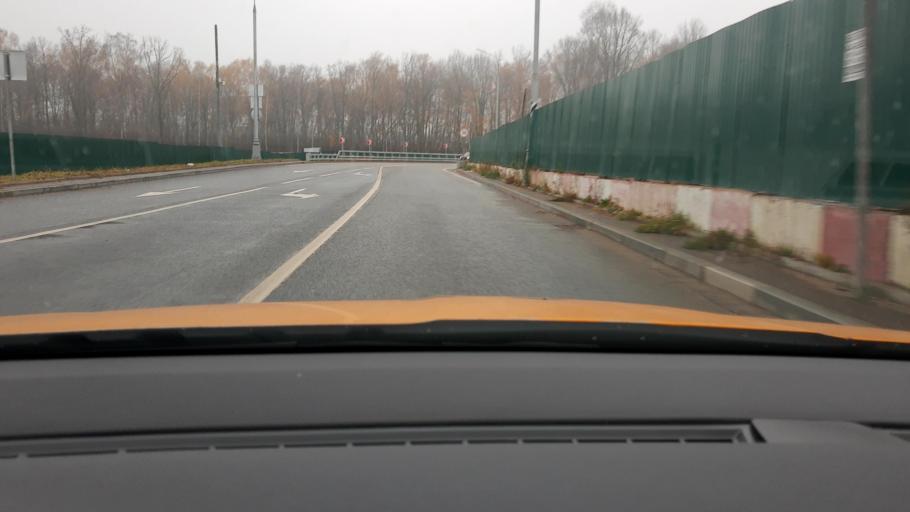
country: RU
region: Moskovskaya
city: Kommunarka
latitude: 55.5592
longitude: 37.4645
